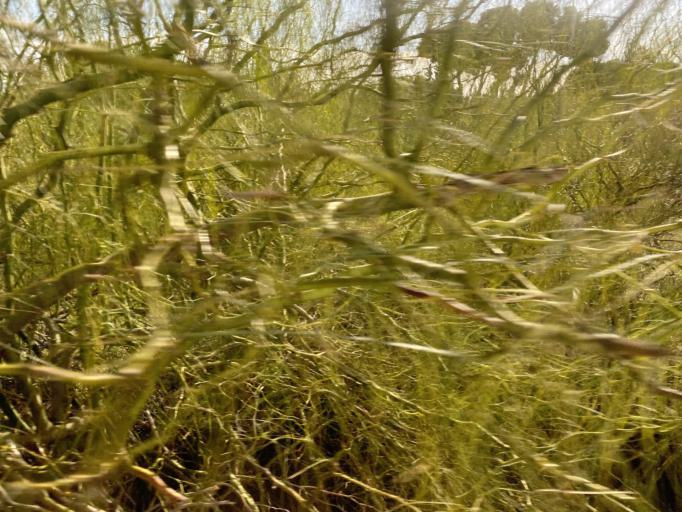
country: ES
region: Catalonia
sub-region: Provincia de Barcelona
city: Sitges
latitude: 41.2351
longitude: 1.7927
